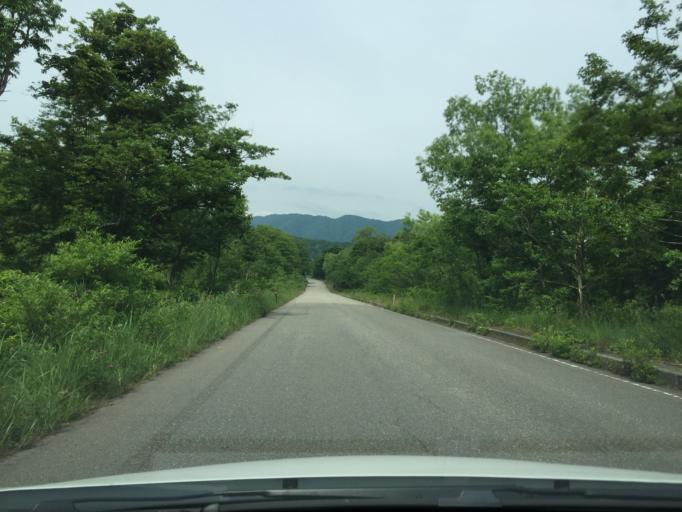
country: JP
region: Fukushima
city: Inawashiro
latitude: 37.6848
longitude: 140.0475
